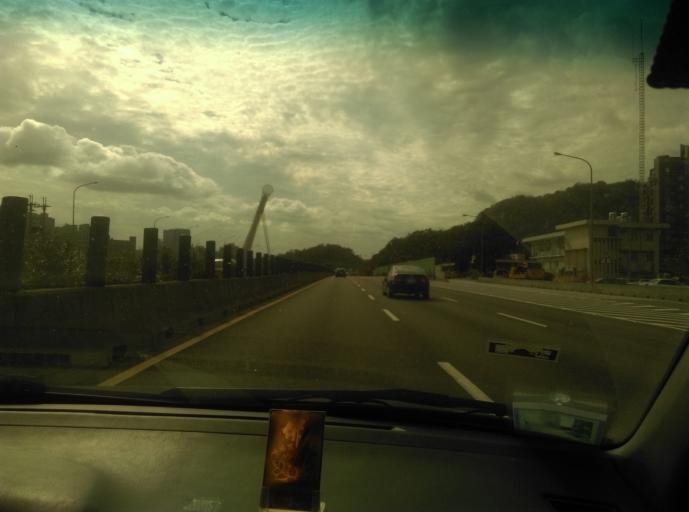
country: TW
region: Taiwan
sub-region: Keelung
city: Keelung
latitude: 25.0798
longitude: 121.6654
